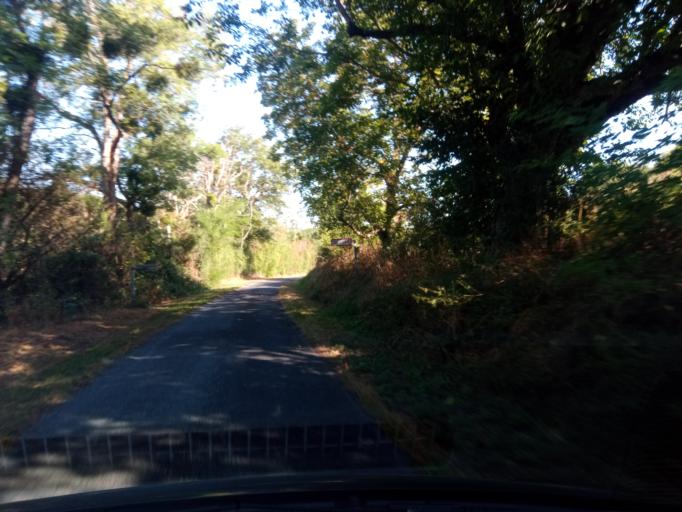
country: FR
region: Poitou-Charentes
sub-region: Departement de la Vienne
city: Saulge
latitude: 46.3761
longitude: 0.8723
